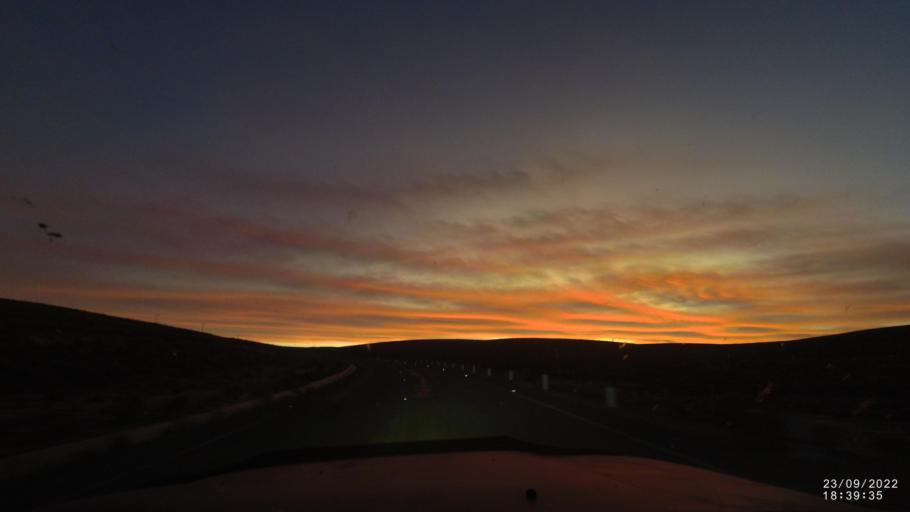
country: BO
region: Oruro
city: Challapata
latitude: -19.4197
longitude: -67.3309
